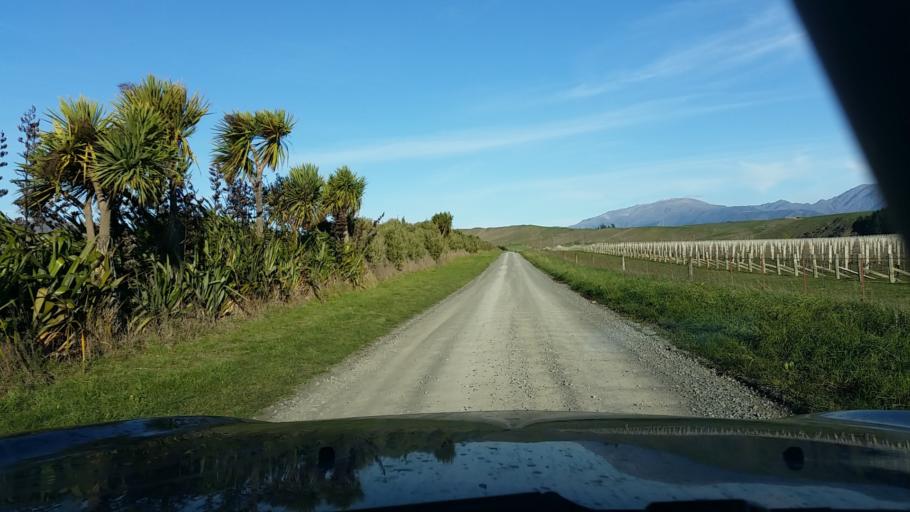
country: NZ
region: Marlborough
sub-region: Marlborough District
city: Blenheim
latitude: -41.7055
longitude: 174.0330
